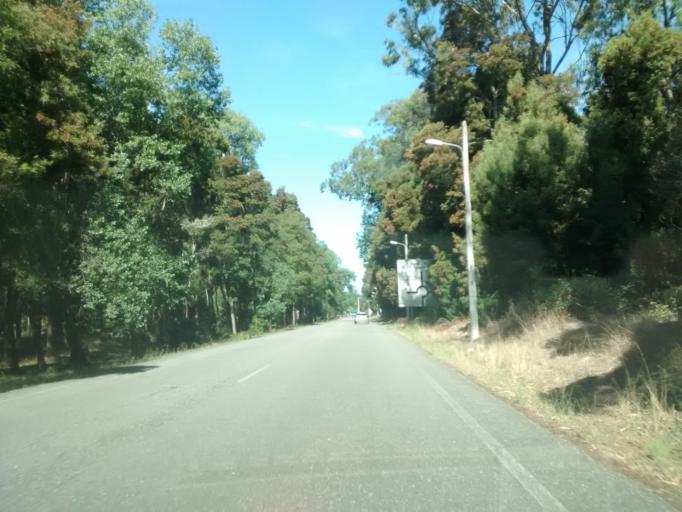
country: PT
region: Coimbra
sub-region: Mira
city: Mira
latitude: 40.4523
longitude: -8.7741
